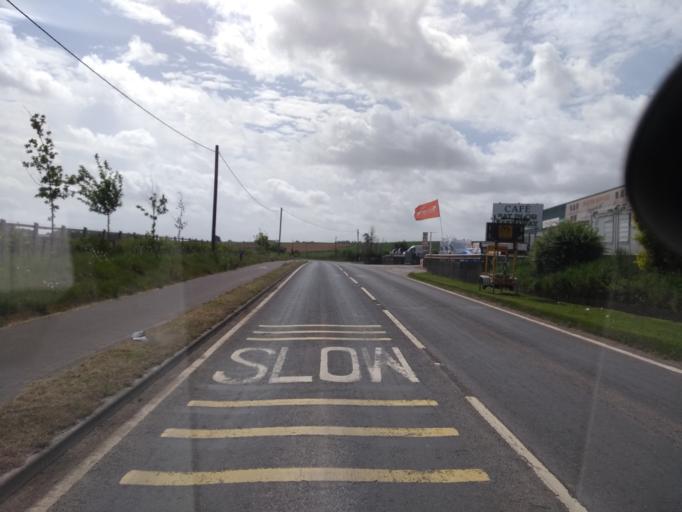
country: GB
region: England
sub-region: Somerset
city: Bridgwater
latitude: 51.1426
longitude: -3.0572
